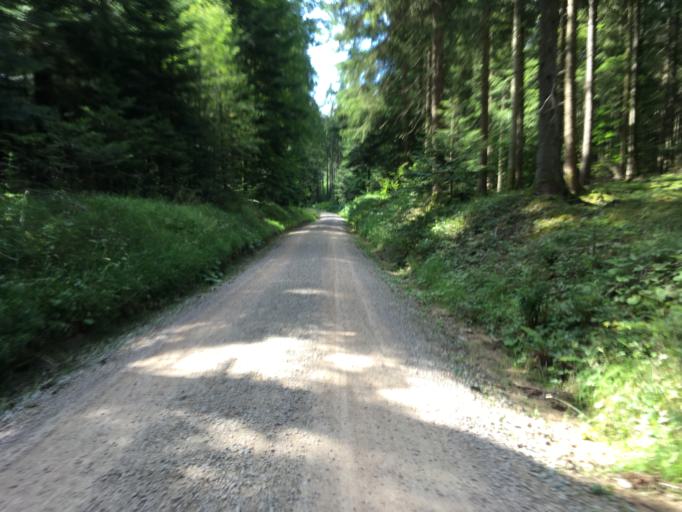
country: DE
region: Baden-Wuerttemberg
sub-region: Karlsruhe Region
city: Lossburg
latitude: 48.4268
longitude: 8.4387
